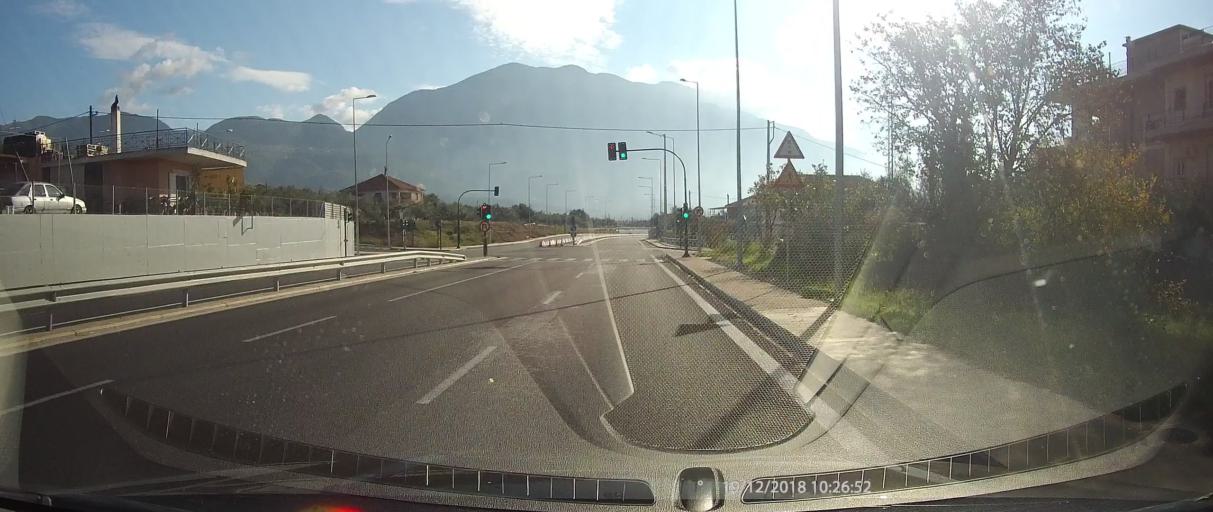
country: GR
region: Peloponnese
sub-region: Nomos Messinias
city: Kalamata
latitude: 37.0419
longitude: 22.1316
